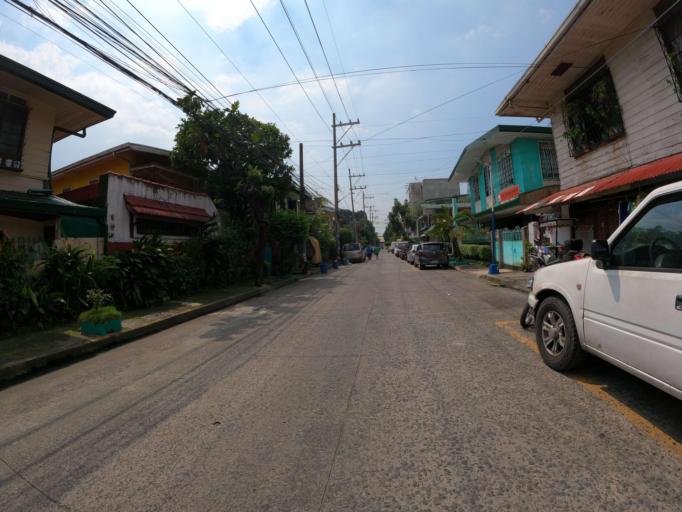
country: PH
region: Metro Manila
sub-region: San Juan
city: San Juan
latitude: 14.5909
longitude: 121.0182
